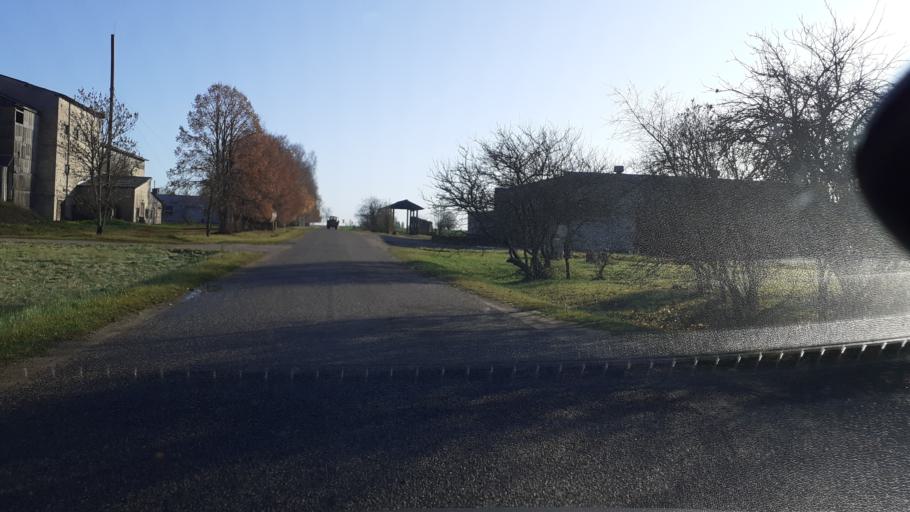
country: LV
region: Kuldigas Rajons
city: Kuldiga
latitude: 56.9973
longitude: 21.8957
